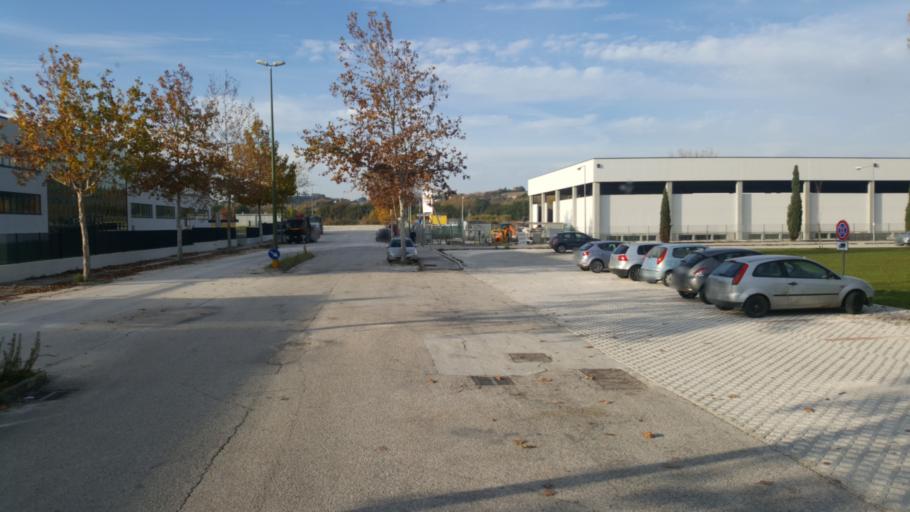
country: IT
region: The Marches
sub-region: Provincia di Ancona
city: Casine
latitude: 43.6480
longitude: 13.1395
